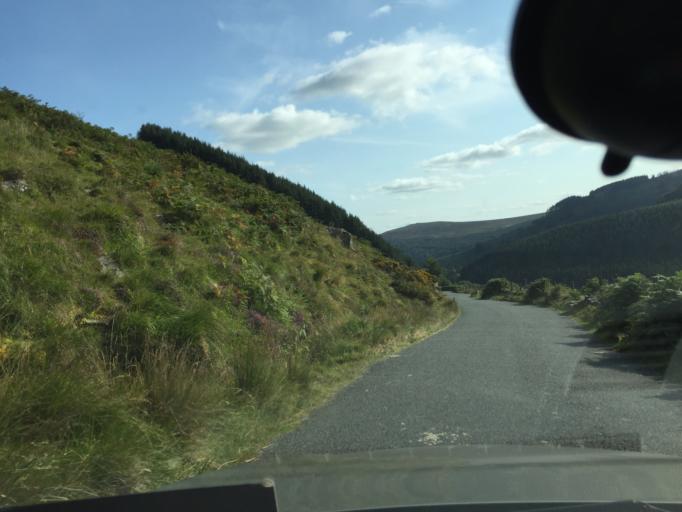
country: IE
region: Leinster
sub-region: Wicklow
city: Rathdrum
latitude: 53.0629
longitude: -6.3326
